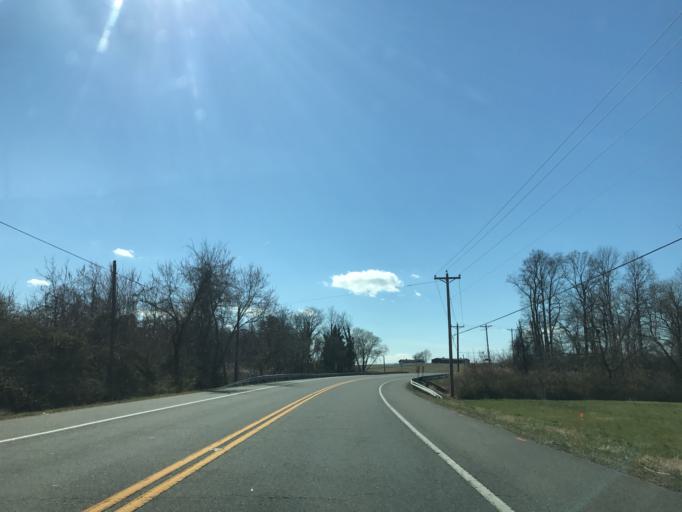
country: US
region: Maryland
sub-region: Kent County
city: Chestertown
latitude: 39.2115
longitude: -76.0978
